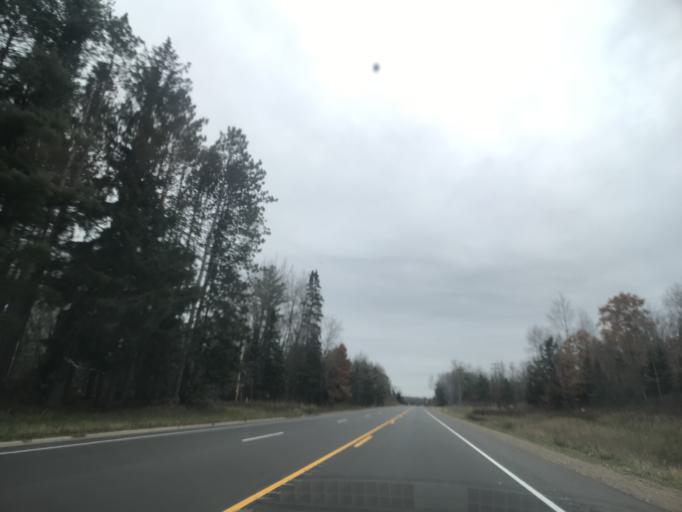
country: US
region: Wisconsin
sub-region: Menominee County
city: Legend Lake
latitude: 45.2542
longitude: -88.5142
